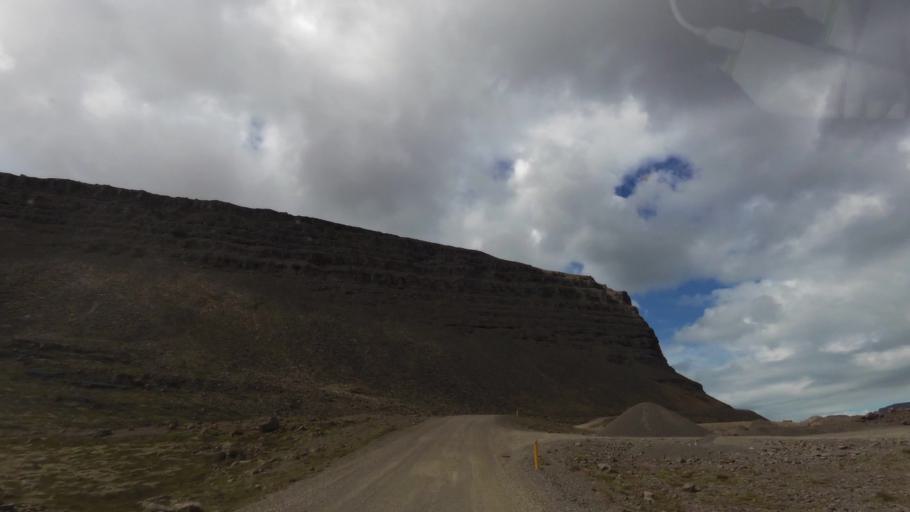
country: IS
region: West
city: Olafsvik
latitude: 65.5762
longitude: -24.0841
